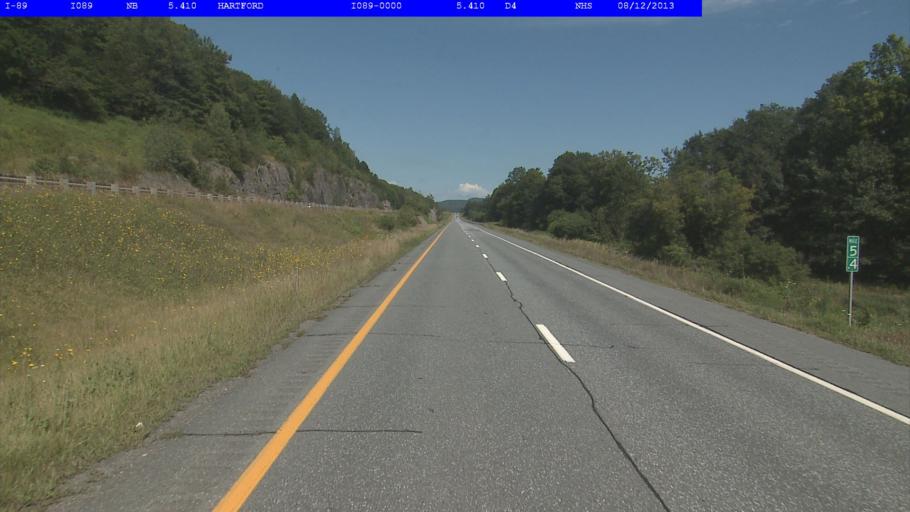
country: US
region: Vermont
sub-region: Windsor County
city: White River Junction
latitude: 43.6843
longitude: -72.4017
